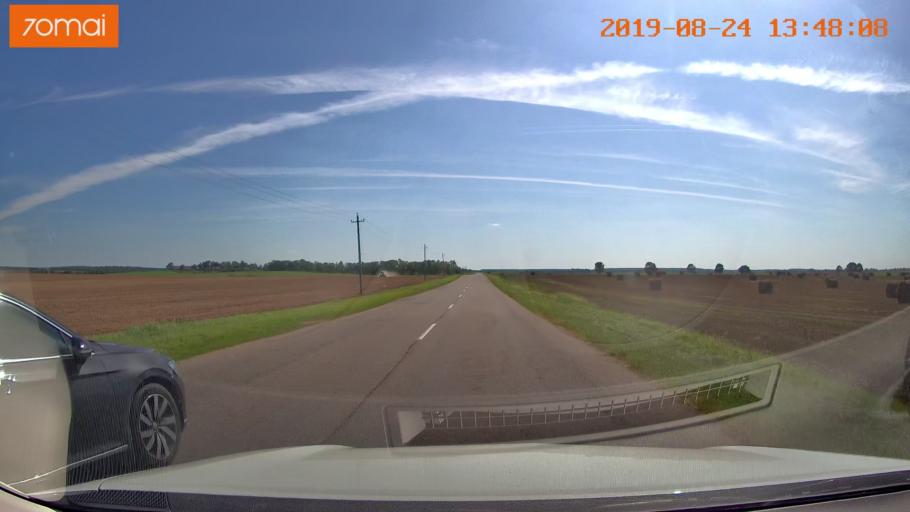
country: BY
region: Minsk
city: Samakhvalavichy
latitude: 53.6519
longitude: 27.5448
